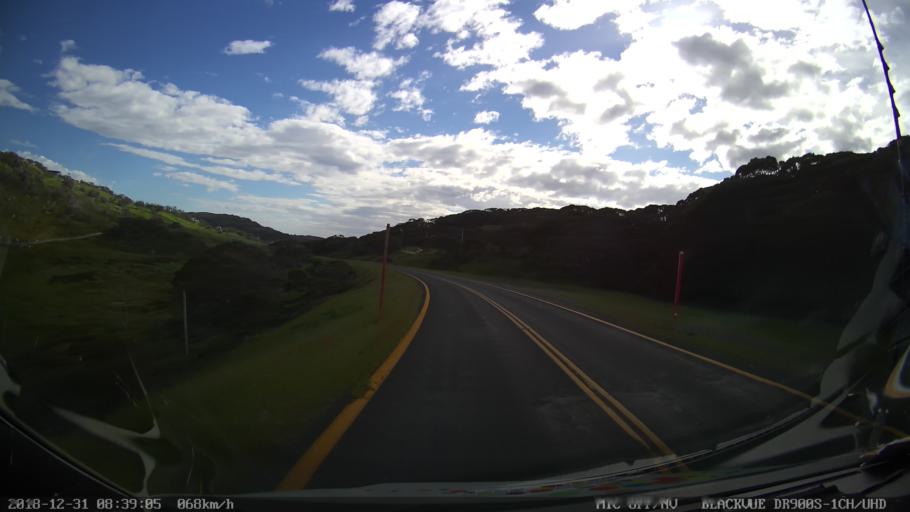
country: AU
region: New South Wales
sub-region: Snowy River
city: Jindabyne
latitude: -36.4112
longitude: 148.4026
